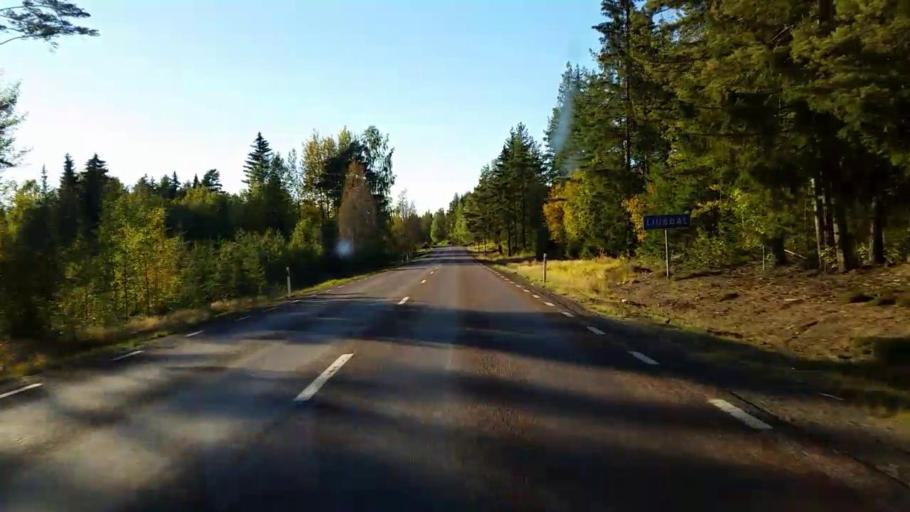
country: SE
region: Gaevleborg
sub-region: Ljusdals Kommun
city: Ljusdal
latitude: 61.8236
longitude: 16.1483
